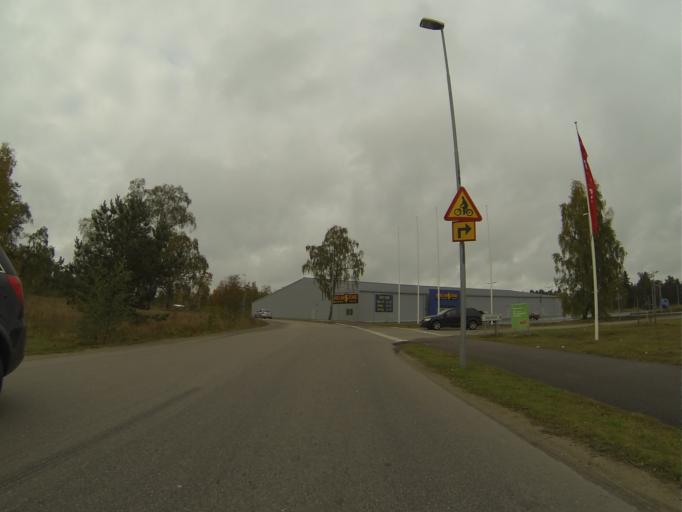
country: SE
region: Skane
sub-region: Sjobo Kommun
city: Sjoebo
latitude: 55.6357
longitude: 13.6802
